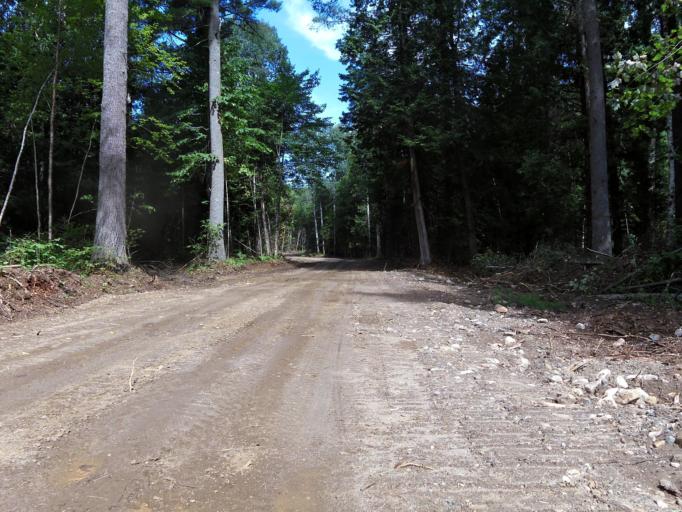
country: CA
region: Ontario
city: Renfrew
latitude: 45.1105
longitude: -76.7241
